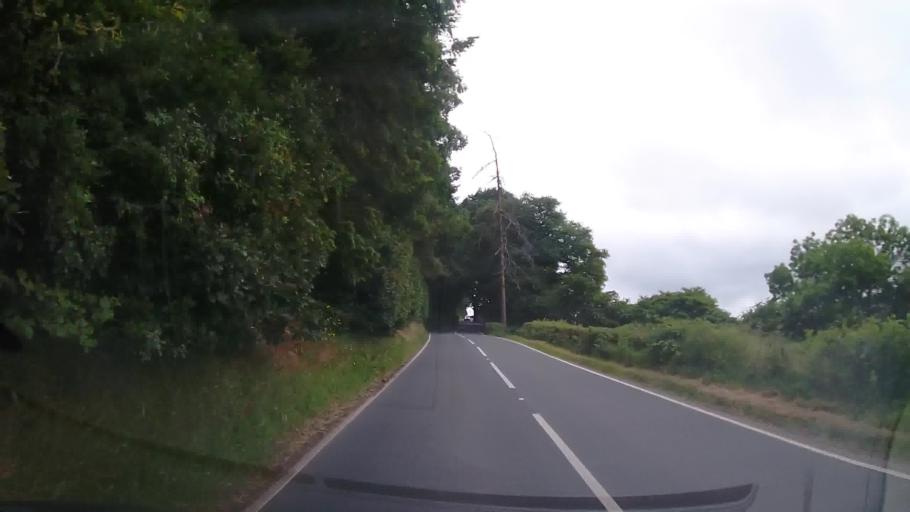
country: GB
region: Wales
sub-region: Denbighshire
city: Llandrillo
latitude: 52.9452
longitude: -3.4180
